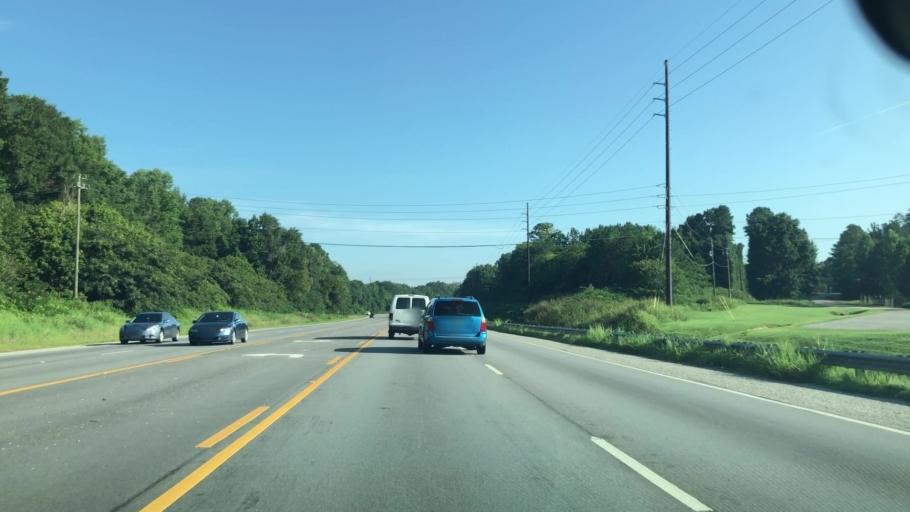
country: US
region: Alabama
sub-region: Calhoun County
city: Bynum
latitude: 33.6037
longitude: -85.9273
